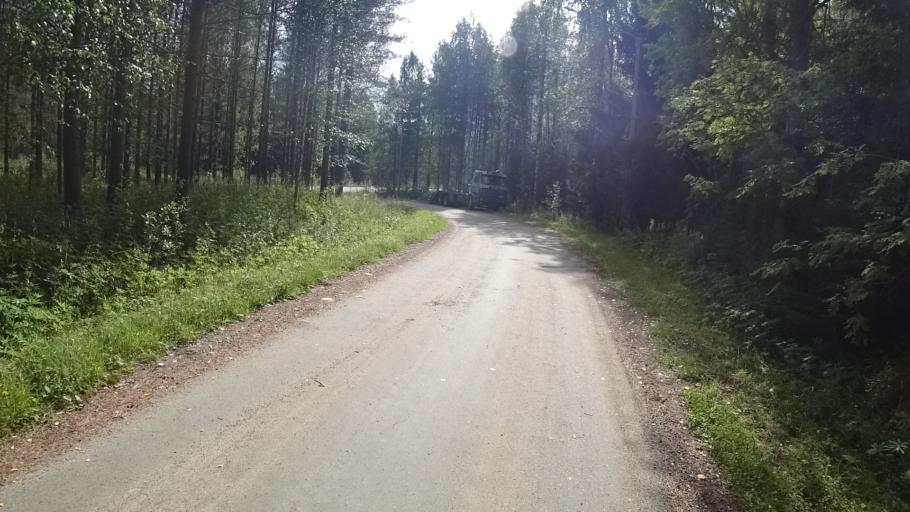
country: FI
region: North Karelia
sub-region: Joensuu
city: Ilomantsi
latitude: 62.6324
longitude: 31.2760
